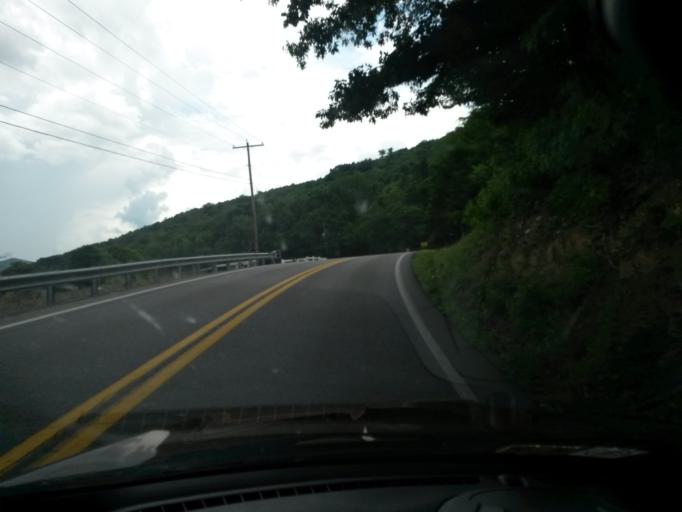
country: US
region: West Virginia
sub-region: Pendleton County
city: Franklin
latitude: 38.6152
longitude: -79.3522
